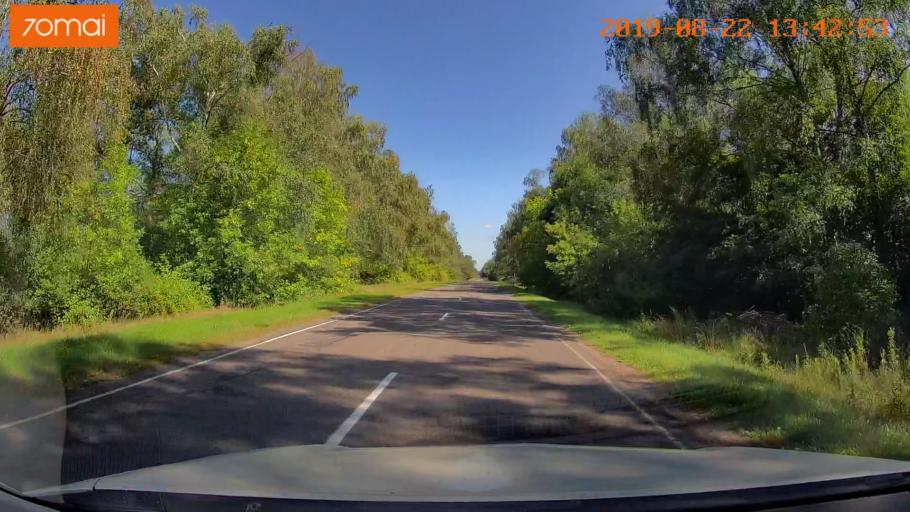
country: BY
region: Mogilev
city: Asipovichy
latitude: 53.2416
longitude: 28.4222
